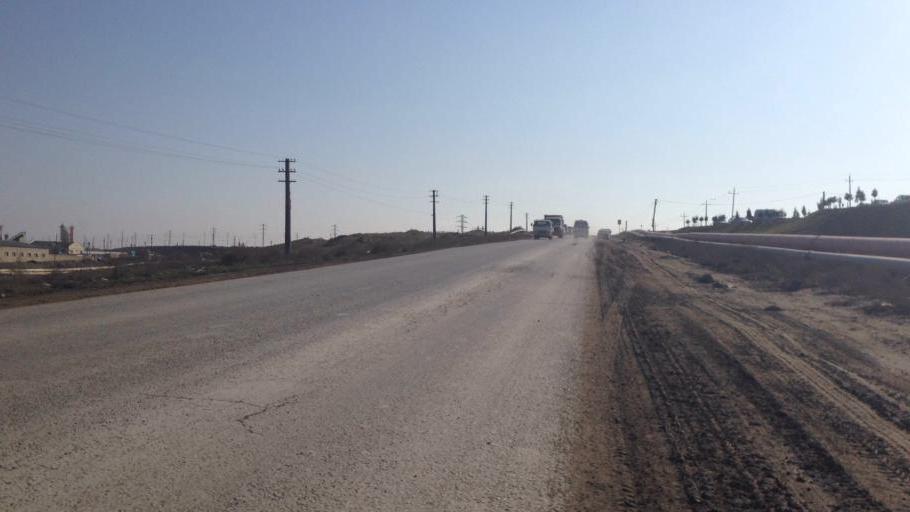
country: AZ
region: Abseron
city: Digah
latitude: 40.4650
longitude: 49.8879
